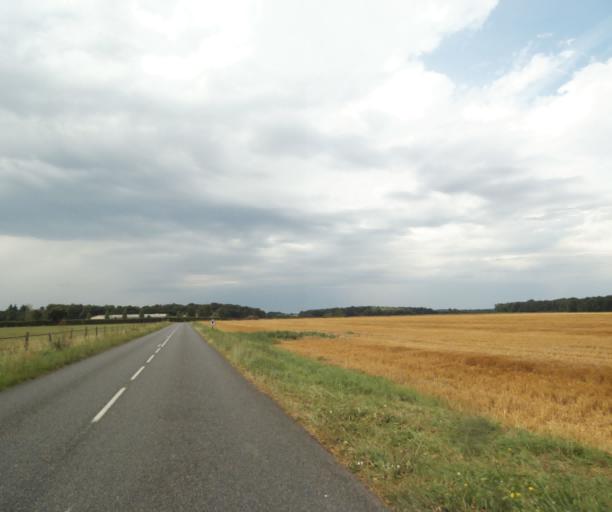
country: FR
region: Ile-de-France
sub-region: Departement de Seine-et-Marne
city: Ponthierry
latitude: 48.5177
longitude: 2.5405
